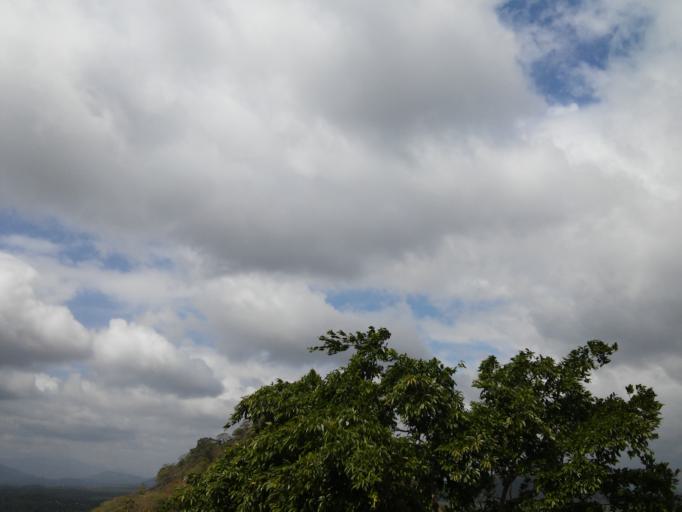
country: LK
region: Central
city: Dambulla
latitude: 7.8560
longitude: 80.6490
